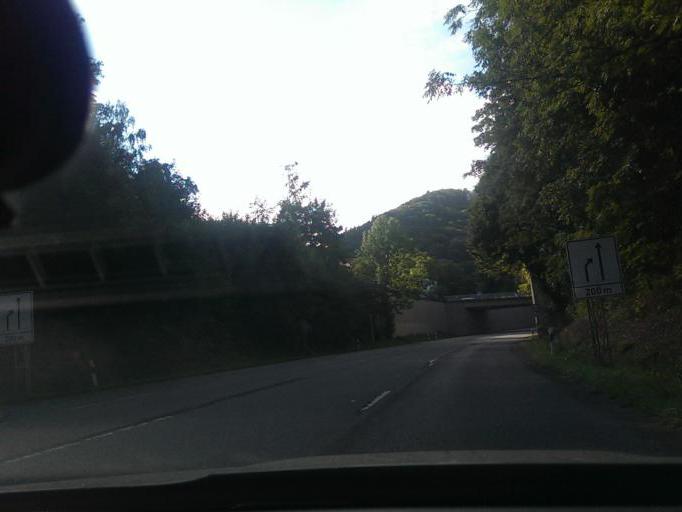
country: DE
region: Lower Saxony
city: Bad Harzburg
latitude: 51.8814
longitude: 10.5650
